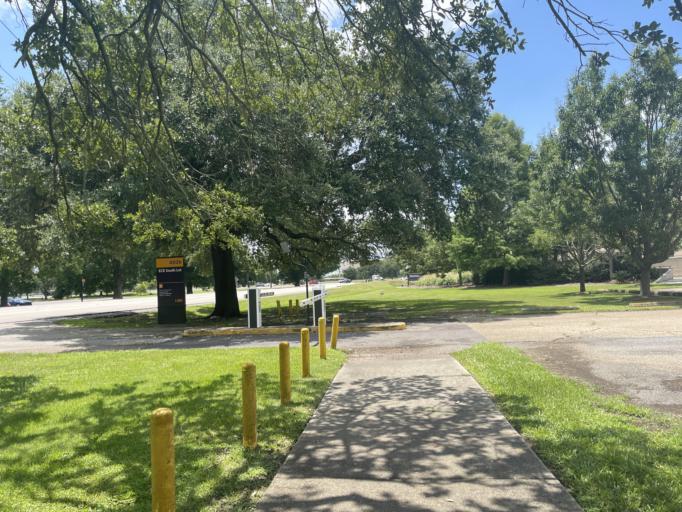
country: US
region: Louisiana
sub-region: West Baton Rouge Parish
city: Port Allen
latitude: 30.4081
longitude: -91.1837
